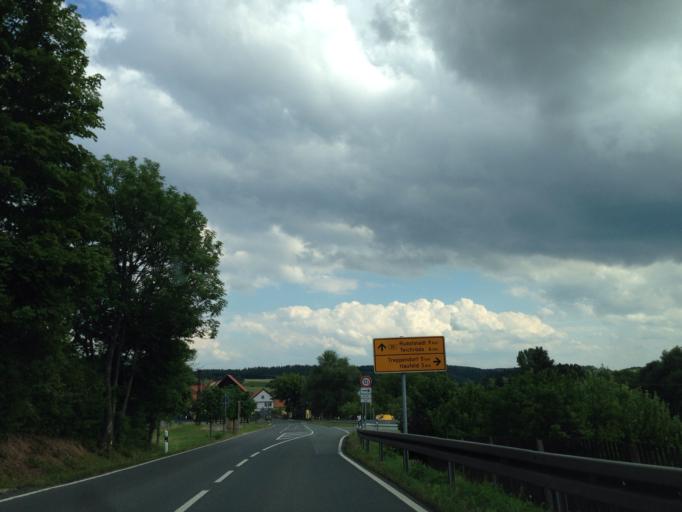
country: DE
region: Thuringia
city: Schwarza
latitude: 50.7902
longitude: 11.3078
